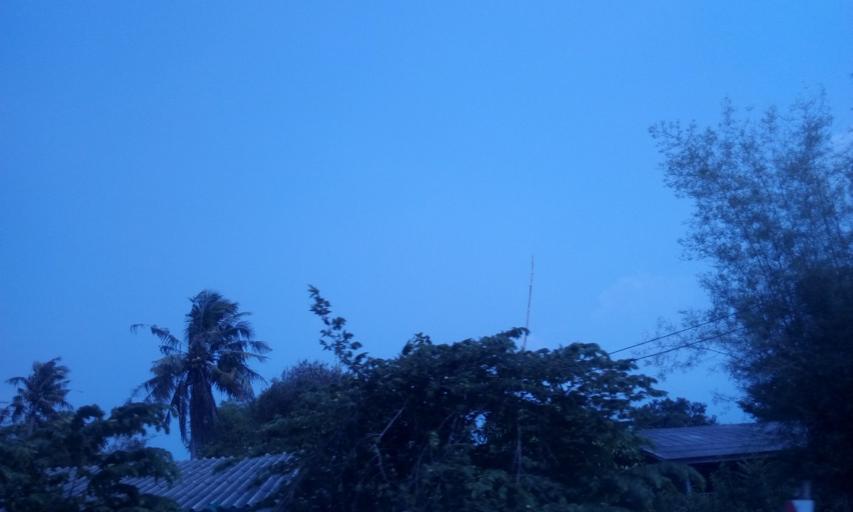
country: TH
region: Chon Buri
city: Phanat Nikhom
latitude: 13.3933
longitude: 101.1926
